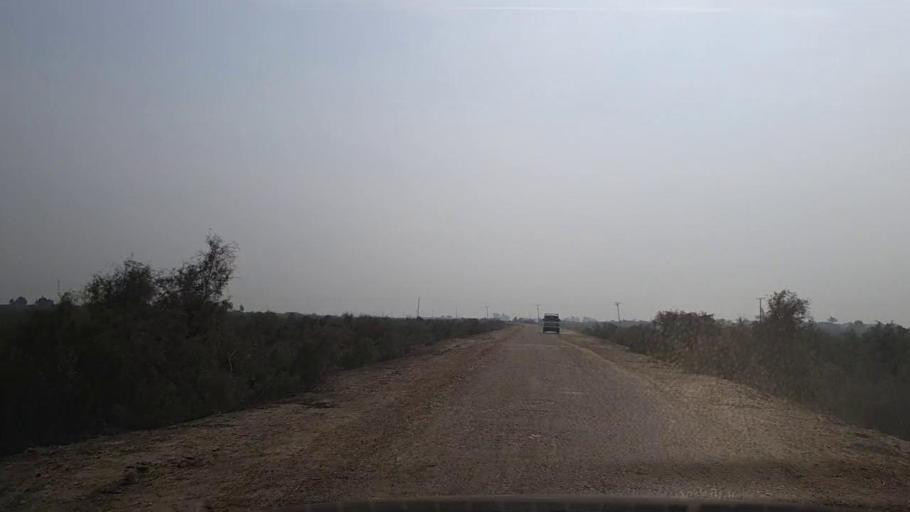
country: PK
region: Sindh
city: Mirpur Sakro
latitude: 24.3982
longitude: 67.7516
